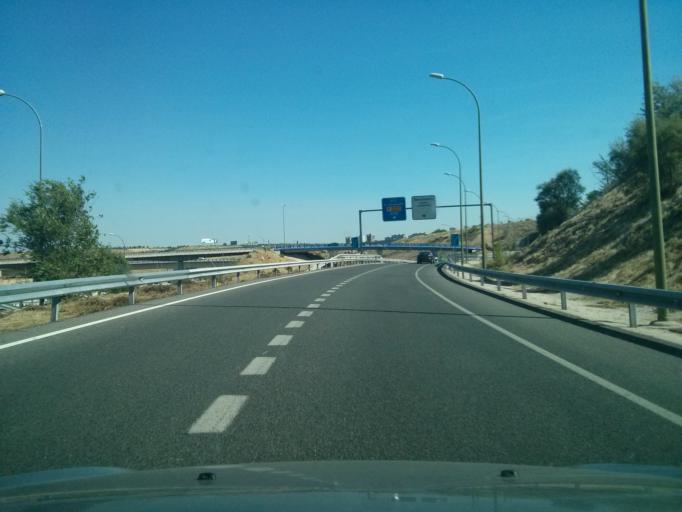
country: ES
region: Madrid
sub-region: Provincia de Madrid
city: Hortaleza
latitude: 40.4979
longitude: -3.6484
